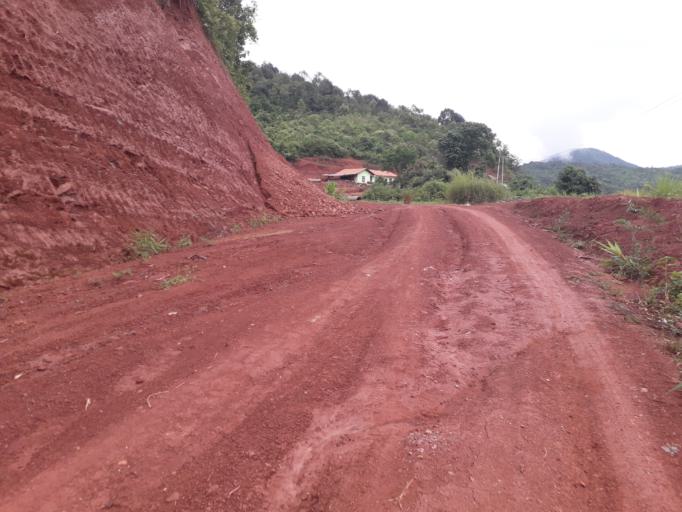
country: CN
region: Yunnan
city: Menglie
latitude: 22.2285
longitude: 101.6230
